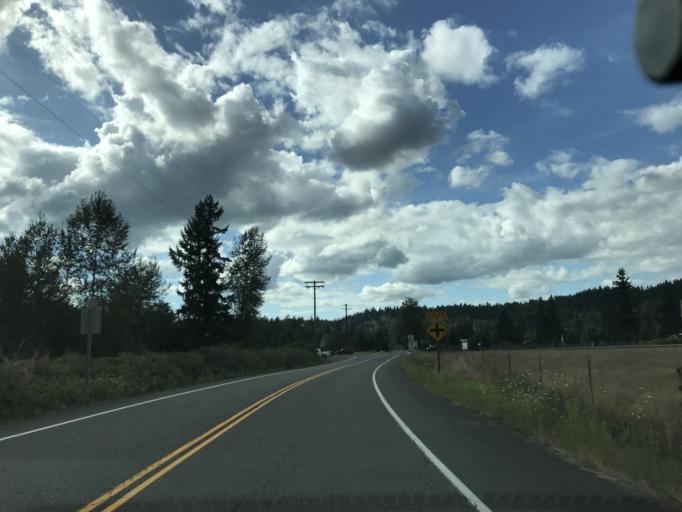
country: US
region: Washington
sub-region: King County
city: Black Diamond
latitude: 47.2829
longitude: -122.0517
